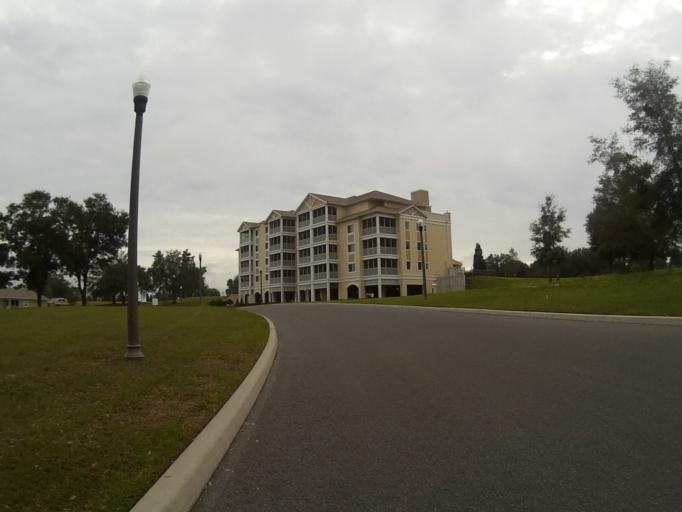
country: US
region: Florida
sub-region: Lake County
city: Umatilla
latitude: 28.9635
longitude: -81.6560
